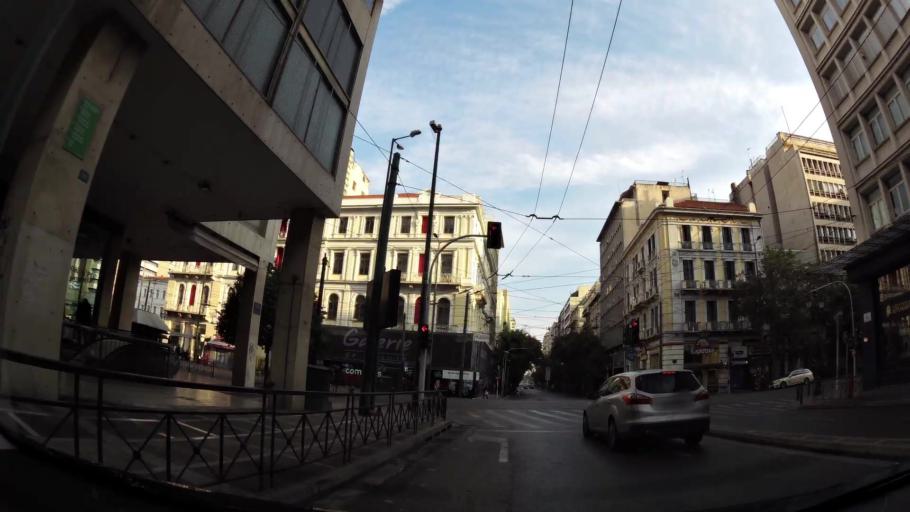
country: GR
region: Attica
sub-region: Nomarchia Athinas
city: Athens
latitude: 37.9835
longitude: 23.7293
